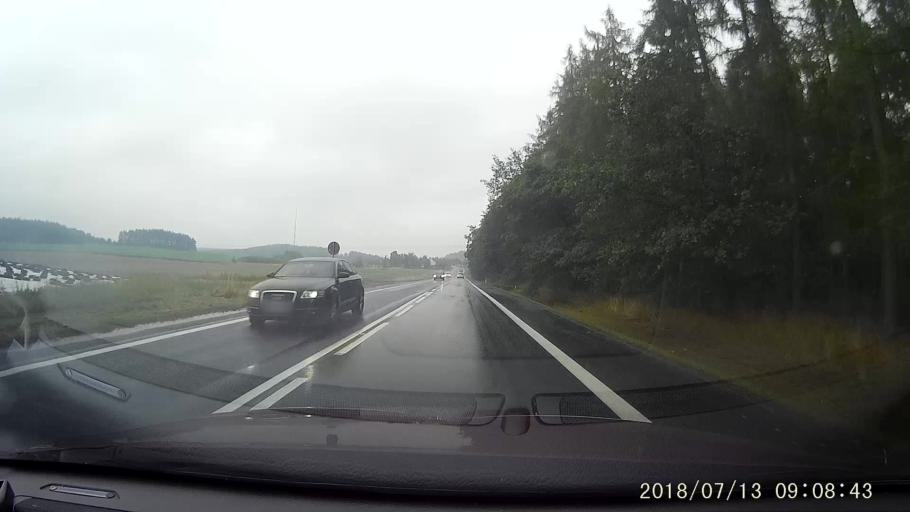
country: PL
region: Lower Silesian Voivodeship
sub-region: Powiat lubanski
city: Siekierczyn
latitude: 51.1551
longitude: 15.1549
